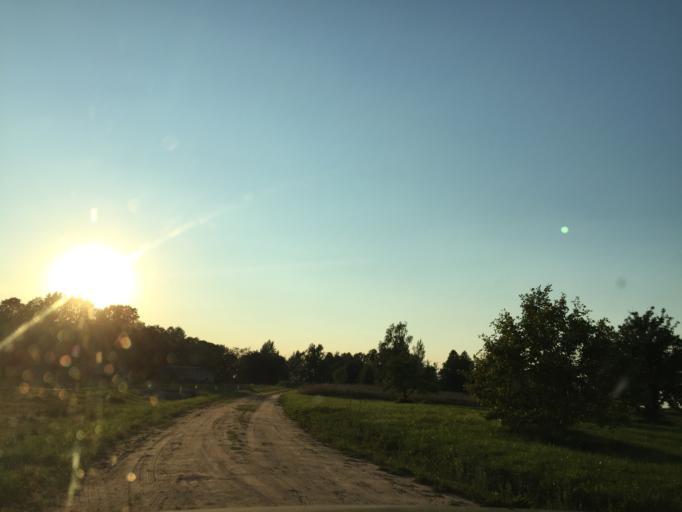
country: LV
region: Limbazu Rajons
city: Limbazi
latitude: 57.5692
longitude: 24.7799
